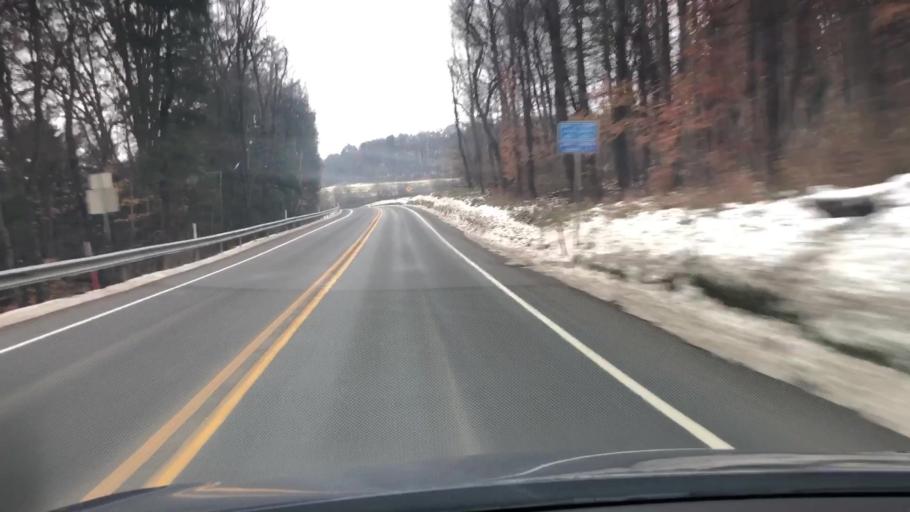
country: US
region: Pennsylvania
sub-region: Jefferson County
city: Brookville
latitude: 41.0410
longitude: -79.2562
